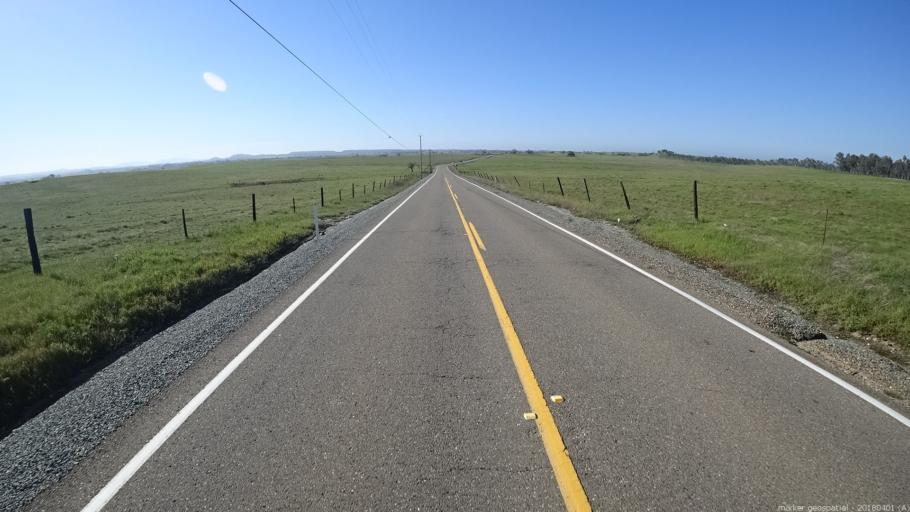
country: US
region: California
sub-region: Sacramento County
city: Rancho Murieta
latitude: 38.4408
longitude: -121.0486
